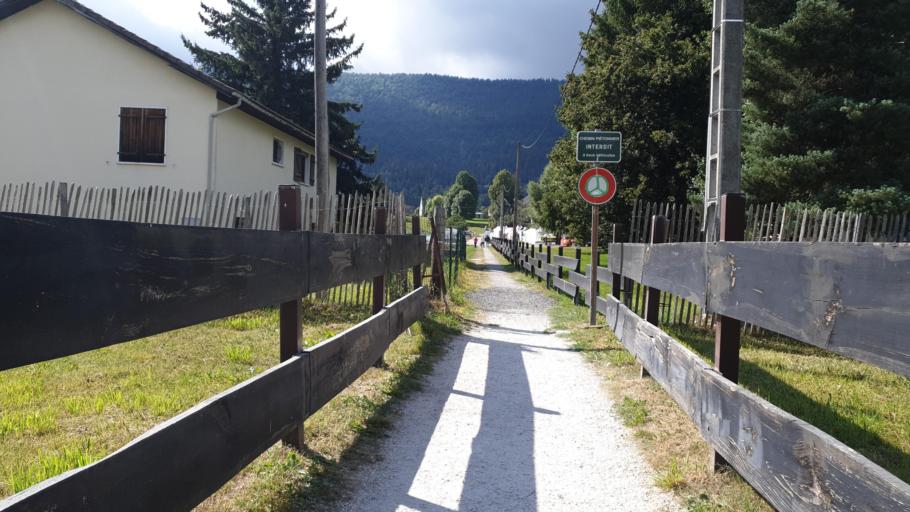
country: FR
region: Rhone-Alpes
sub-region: Departement de l'Isere
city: Autrans
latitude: 45.1755
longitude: 5.5411
